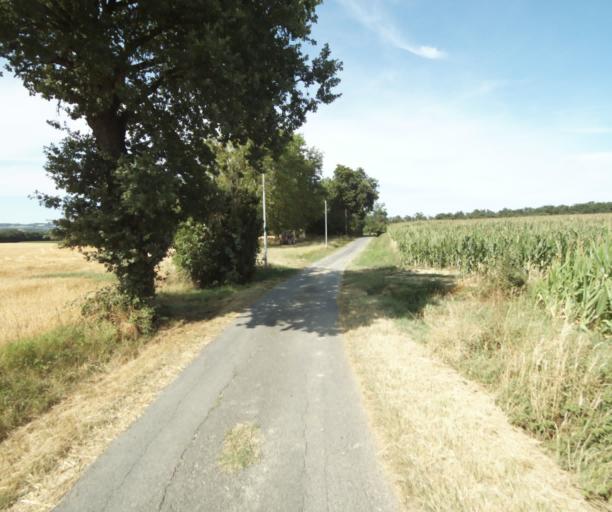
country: FR
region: Midi-Pyrenees
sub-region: Departement du Tarn
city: Soual
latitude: 43.5124
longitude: 2.0860
